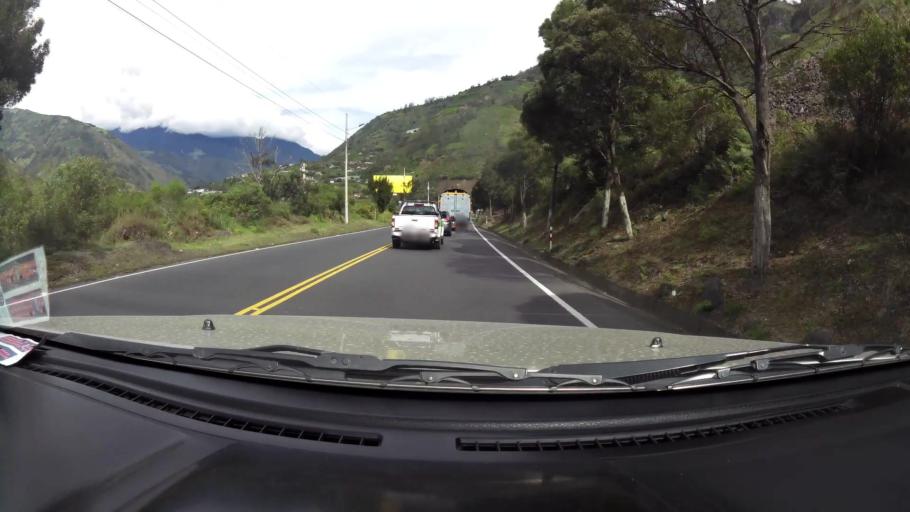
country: EC
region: Tungurahua
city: Banos
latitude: -1.4057
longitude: -78.4599
